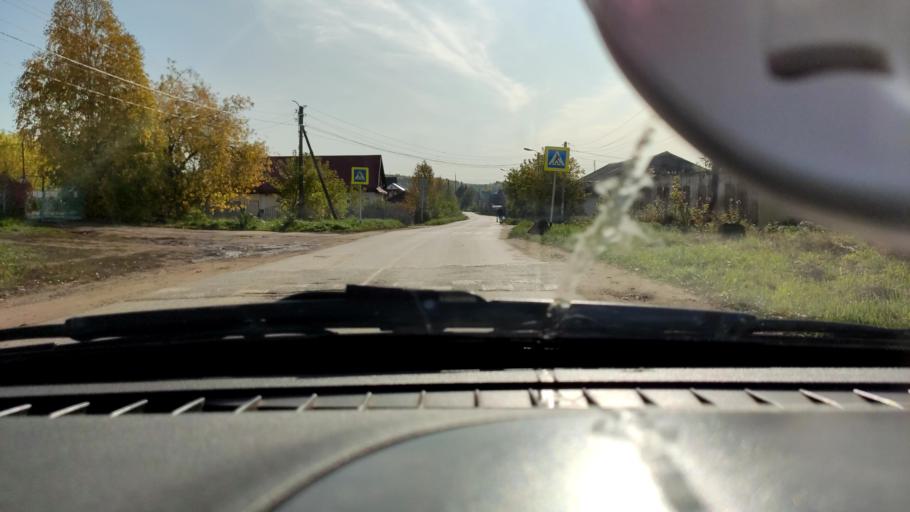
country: RU
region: Perm
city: Overyata
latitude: 58.0833
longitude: 55.8786
